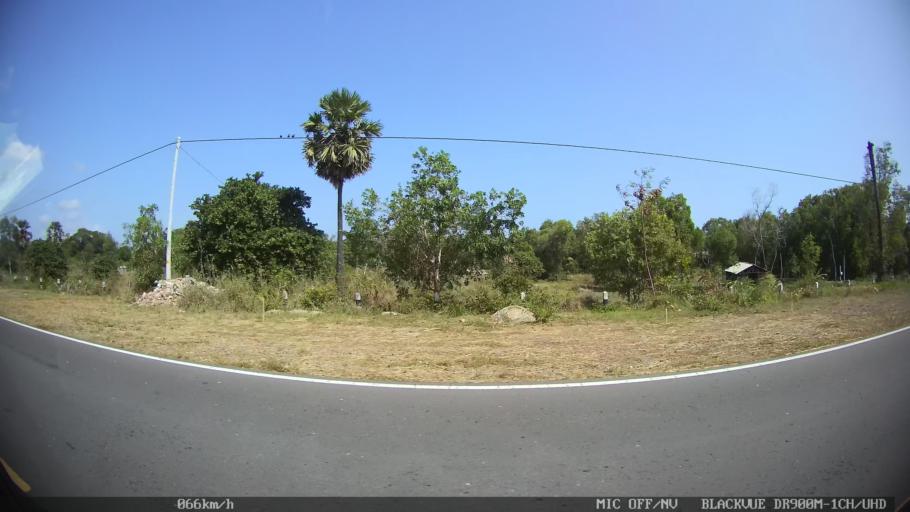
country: ID
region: Daerah Istimewa Yogyakarta
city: Bambanglipuro
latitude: -8.0109
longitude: 110.3055
